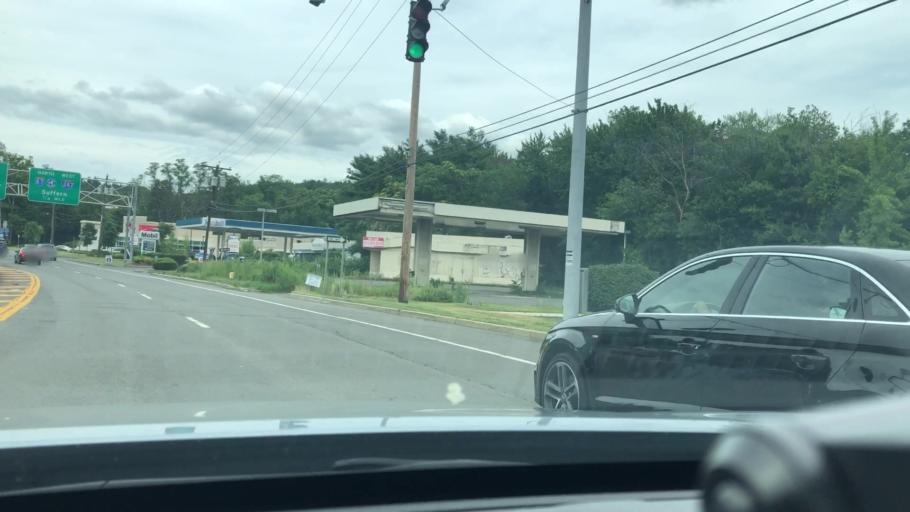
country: US
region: New York
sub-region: Rockland County
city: Valley Cottage
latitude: 41.0971
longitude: -73.9504
